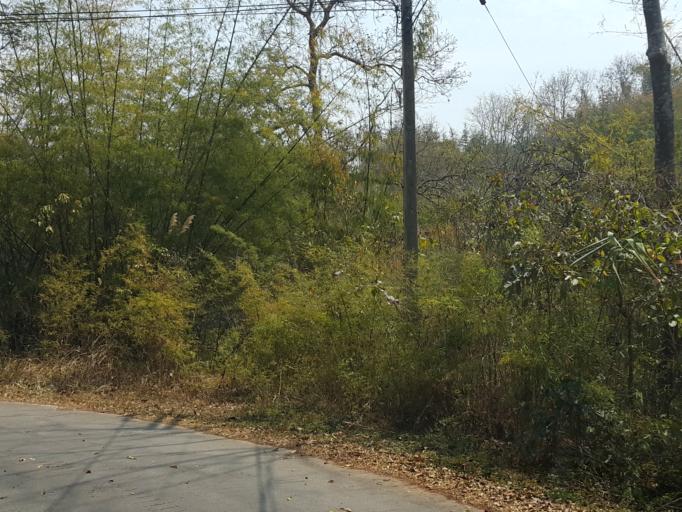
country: TH
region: Lampang
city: Mueang Pan
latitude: 18.8183
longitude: 99.4439
